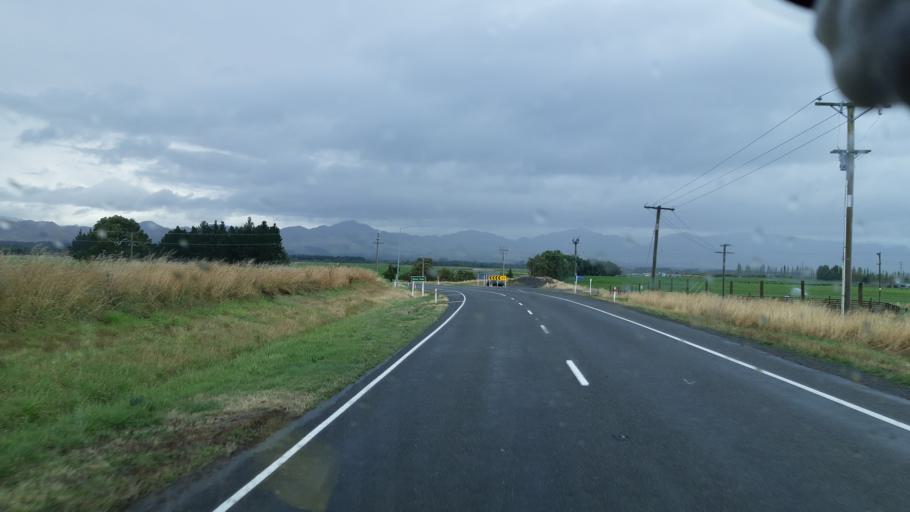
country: NZ
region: Canterbury
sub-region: Hurunui District
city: Amberley
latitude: -42.7192
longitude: 172.8678
